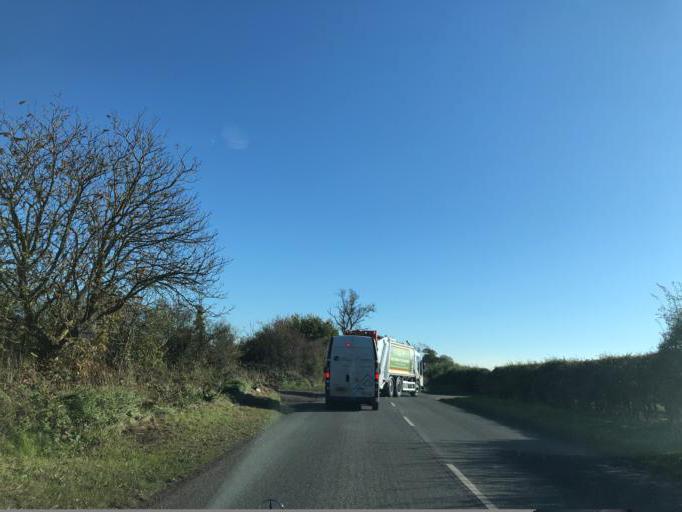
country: GB
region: England
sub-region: Warwickshire
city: Royal Leamington Spa
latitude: 52.2544
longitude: -1.5241
